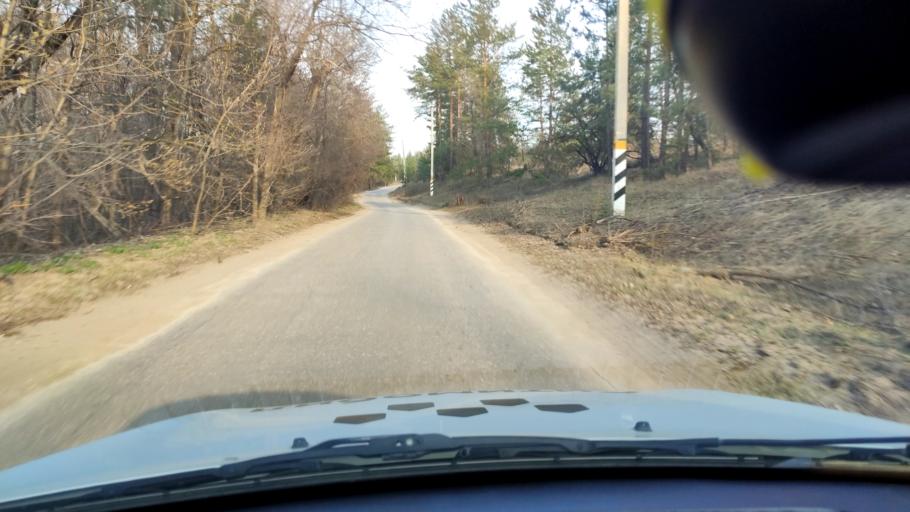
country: RU
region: Samara
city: Zhigulevsk
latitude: 53.4580
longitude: 49.5940
